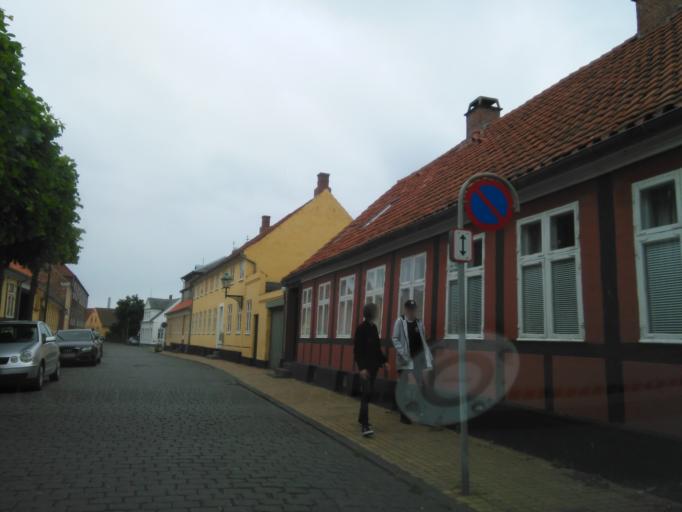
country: DK
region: Capital Region
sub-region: Bornholm Kommune
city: Ronne
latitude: 55.1013
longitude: 14.6956
